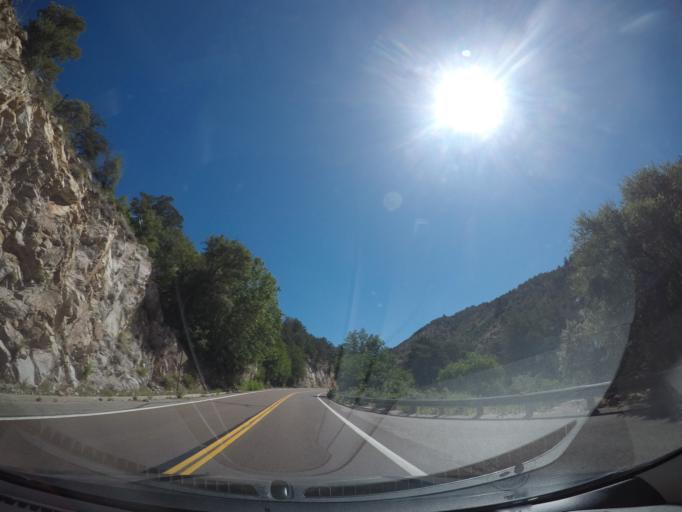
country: US
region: Arizona
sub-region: Pima County
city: Tanque Verde
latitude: 32.3636
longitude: -110.7128
